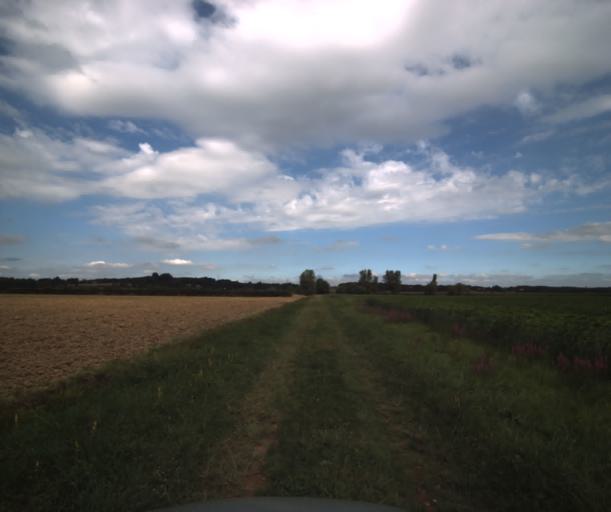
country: FR
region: Midi-Pyrenees
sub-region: Departement de la Haute-Garonne
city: Lherm
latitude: 43.3980
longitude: 1.2278
